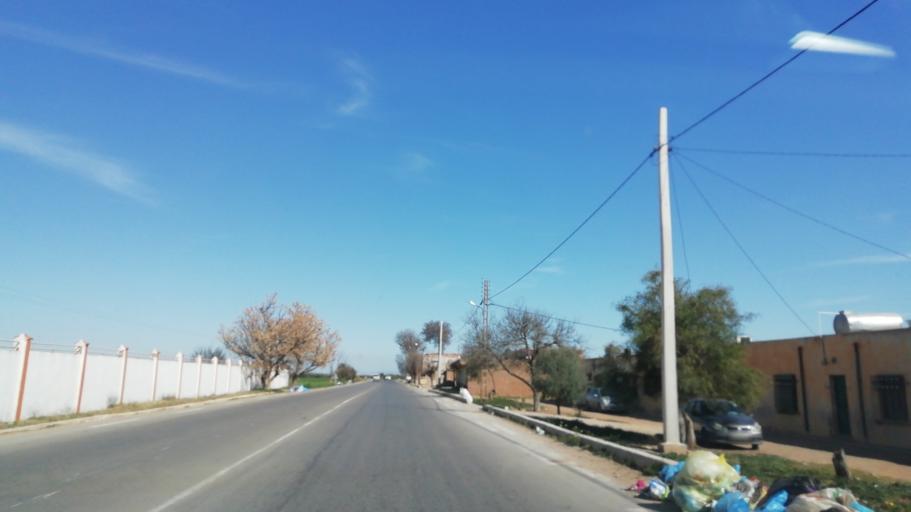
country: DZ
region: Mascara
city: Oued el Abtal
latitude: 35.4241
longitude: 0.4501
